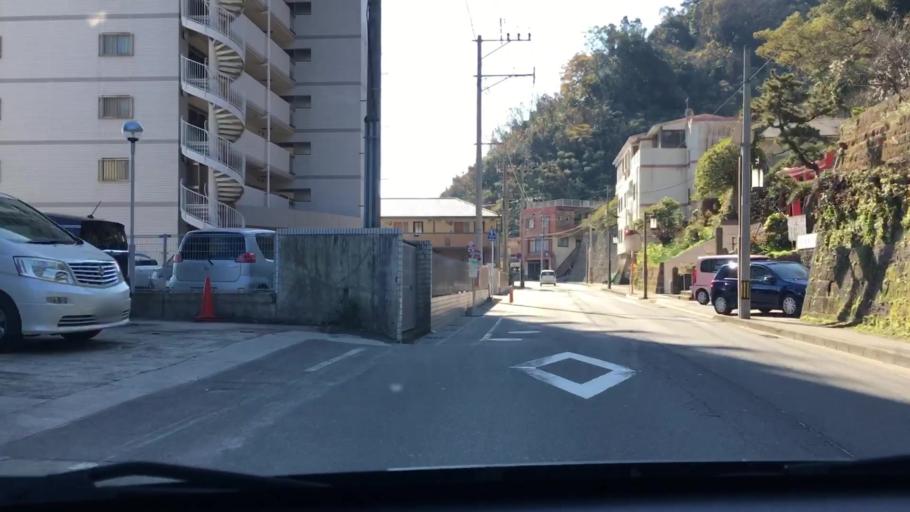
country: JP
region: Kagoshima
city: Kagoshima-shi
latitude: 31.6142
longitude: 130.5746
